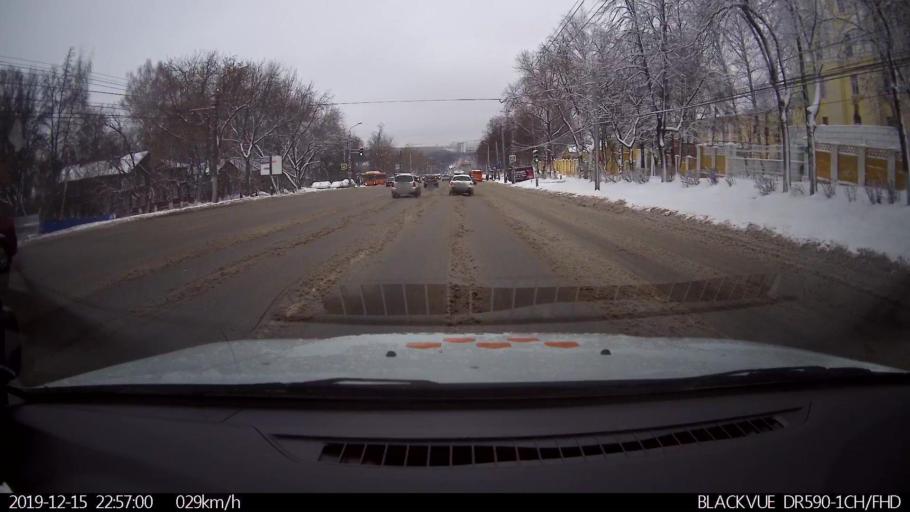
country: RU
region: Nizjnij Novgorod
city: Nizhniy Novgorod
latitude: 56.2482
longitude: 43.9667
